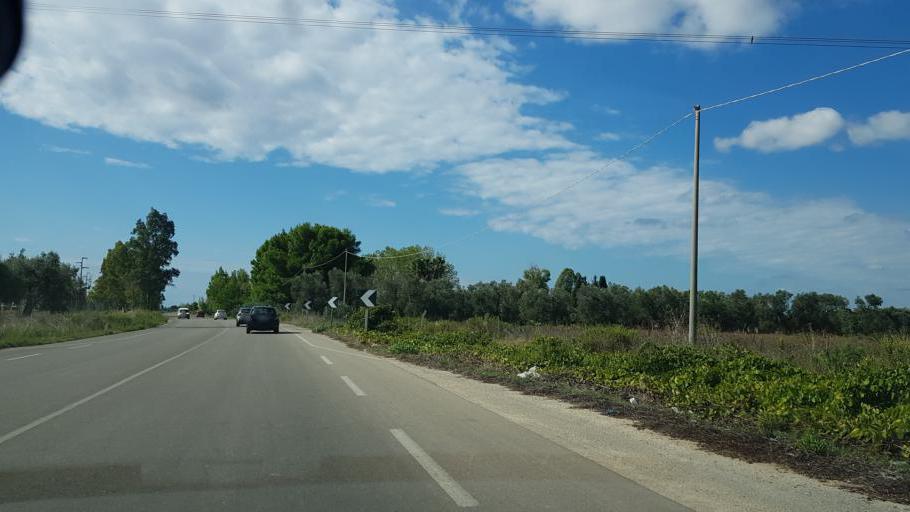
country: IT
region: Apulia
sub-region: Provincia di Lecce
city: Leverano
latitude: 40.3084
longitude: 18.0184
